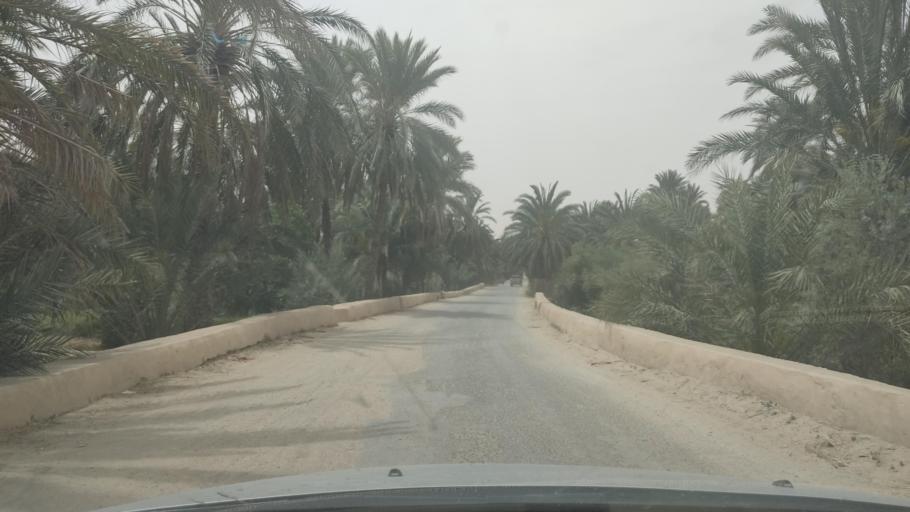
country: TN
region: Gafsa
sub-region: Gafsa Municipality
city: Gafsa
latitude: 34.3283
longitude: 8.9522
